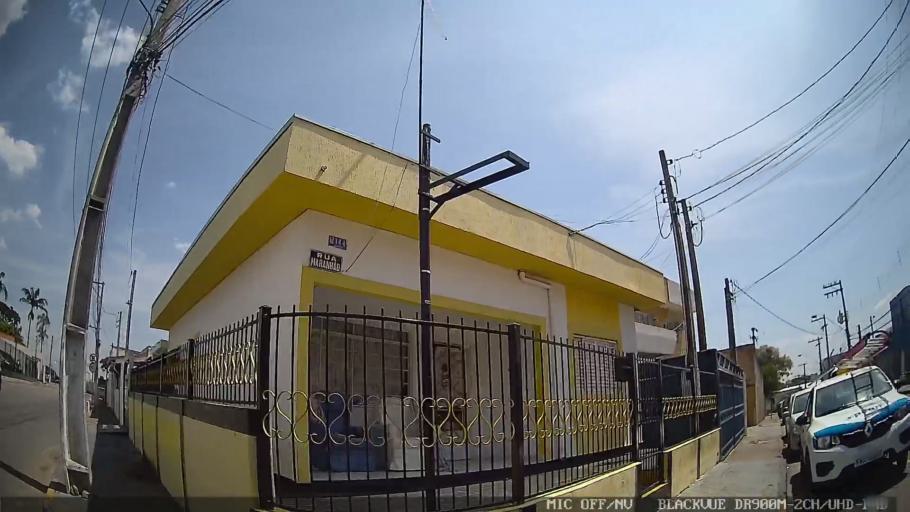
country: BR
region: Sao Paulo
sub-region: Itupeva
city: Itupeva
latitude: -23.2460
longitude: -47.0564
